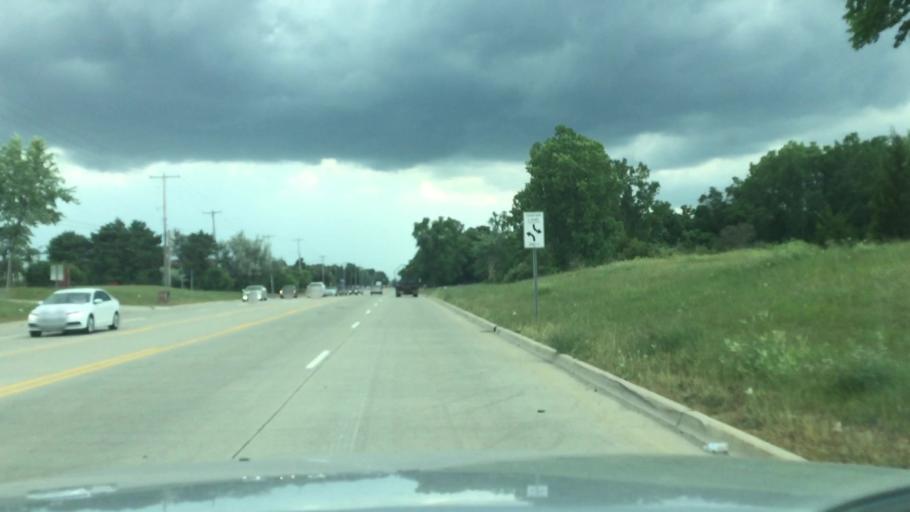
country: US
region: Michigan
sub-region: Genesee County
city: Flushing
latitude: 43.0307
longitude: -83.7736
